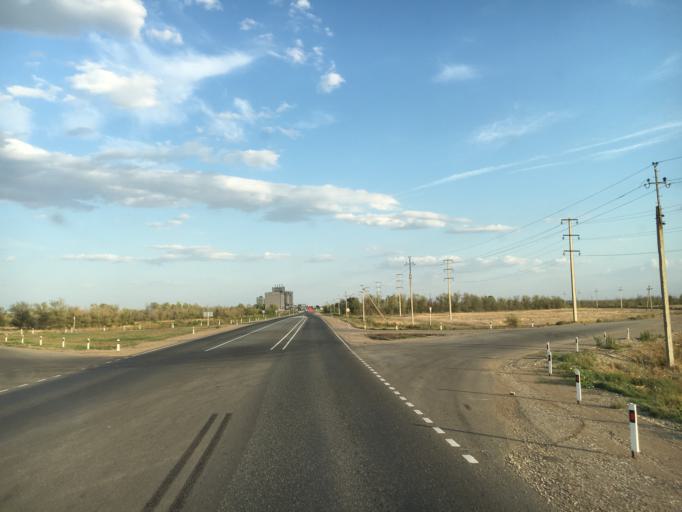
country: KZ
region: Aqtoebe
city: Aqtobe
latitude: 50.2047
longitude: 57.2220
